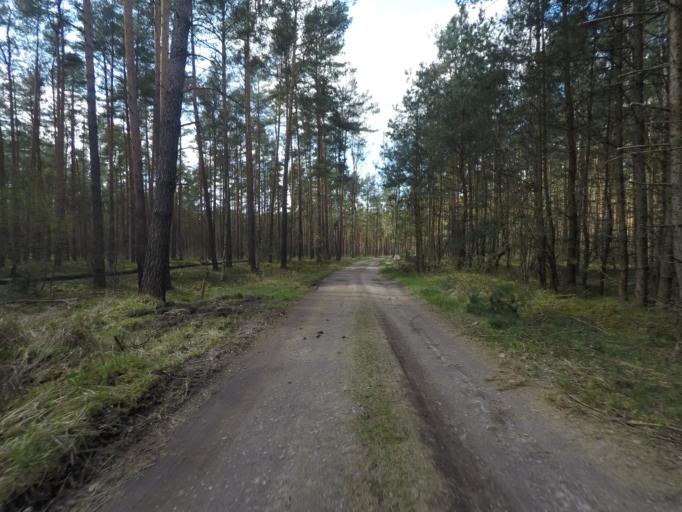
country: DE
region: Brandenburg
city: Melchow
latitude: 52.8187
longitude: 13.6922
